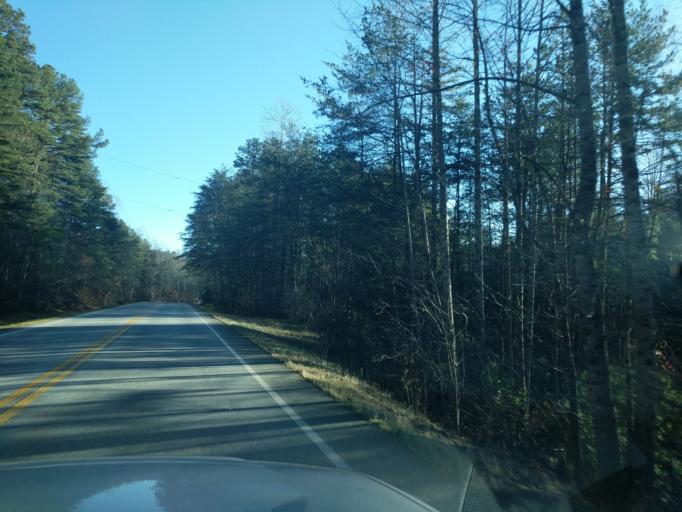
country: US
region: Georgia
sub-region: Rabun County
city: Clayton
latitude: 34.8237
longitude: -83.3210
